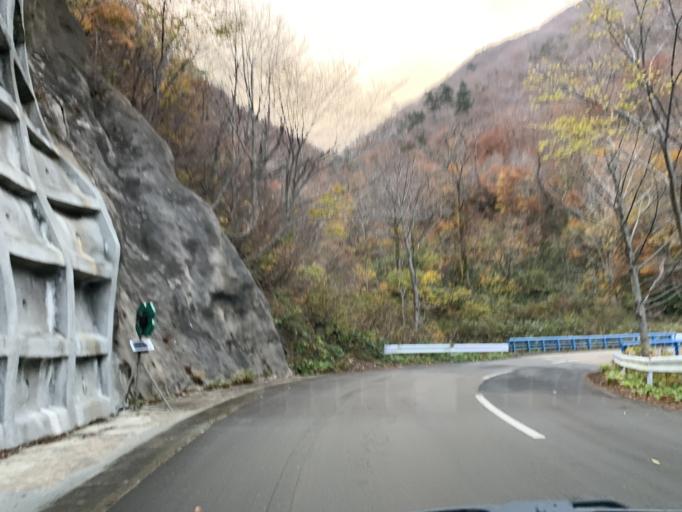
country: JP
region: Iwate
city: Mizusawa
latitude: 39.1267
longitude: 140.8294
